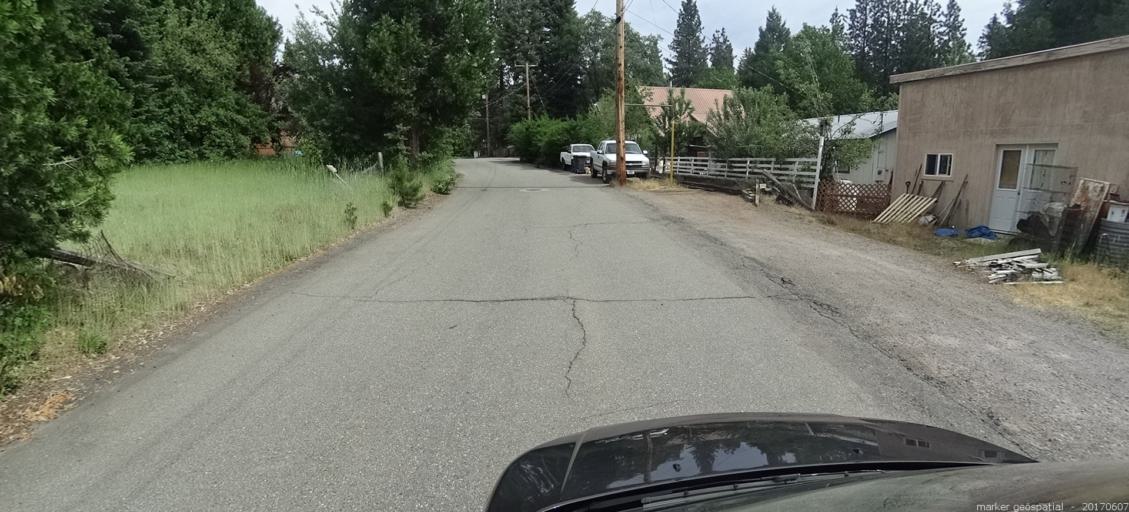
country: US
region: California
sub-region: Siskiyou County
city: McCloud
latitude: 41.2515
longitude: -122.1416
